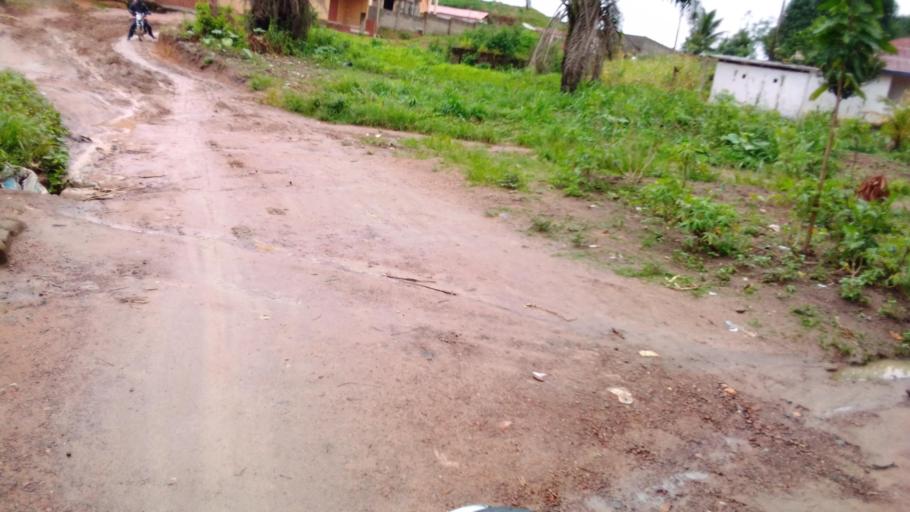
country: SL
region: Eastern Province
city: Kenema
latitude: 7.8740
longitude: -11.1739
